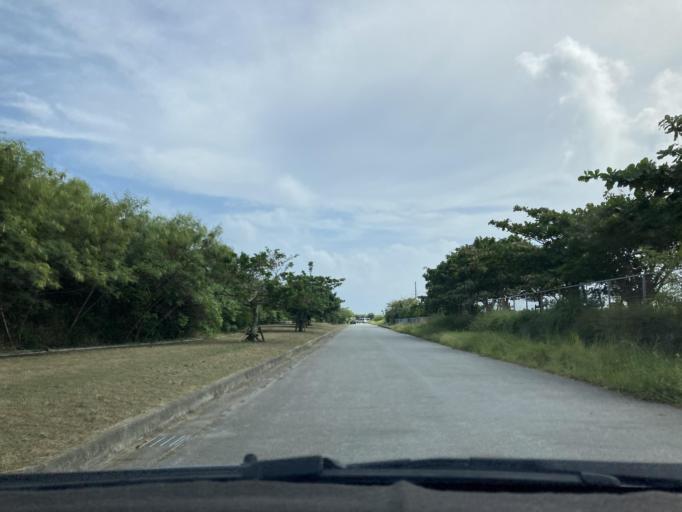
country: JP
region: Okinawa
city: Ginowan
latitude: 26.1507
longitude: 127.8086
